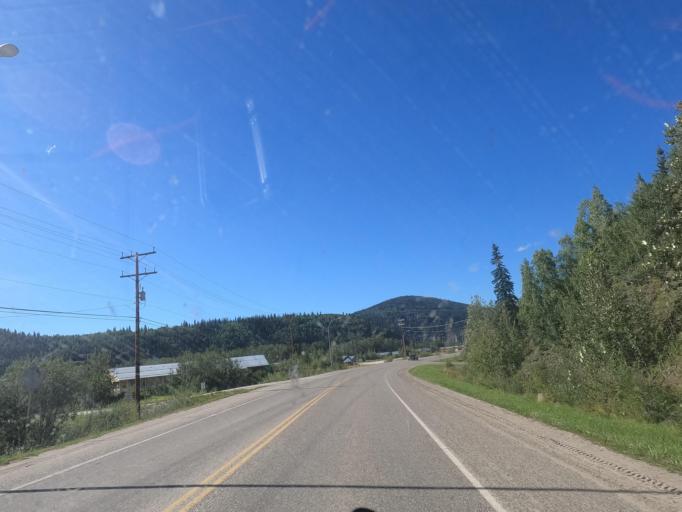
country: CA
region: Yukon
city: Dawson City
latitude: 64.0438
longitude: -139.4150
